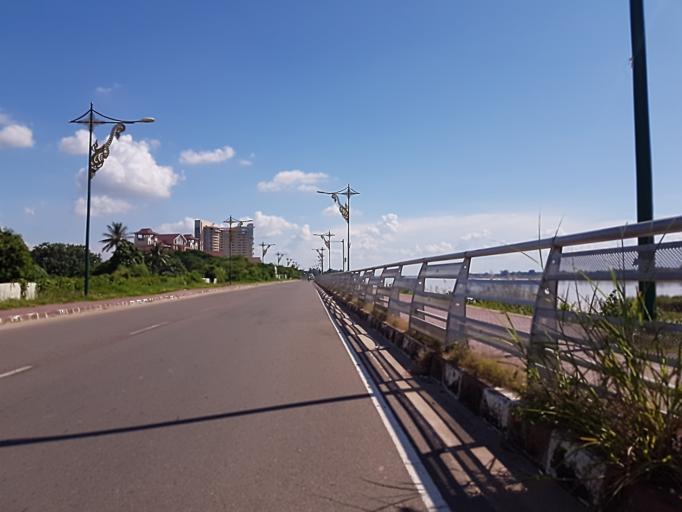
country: LA
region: Vientiane
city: Vientiane
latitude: 17.9486
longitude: 102.6156
